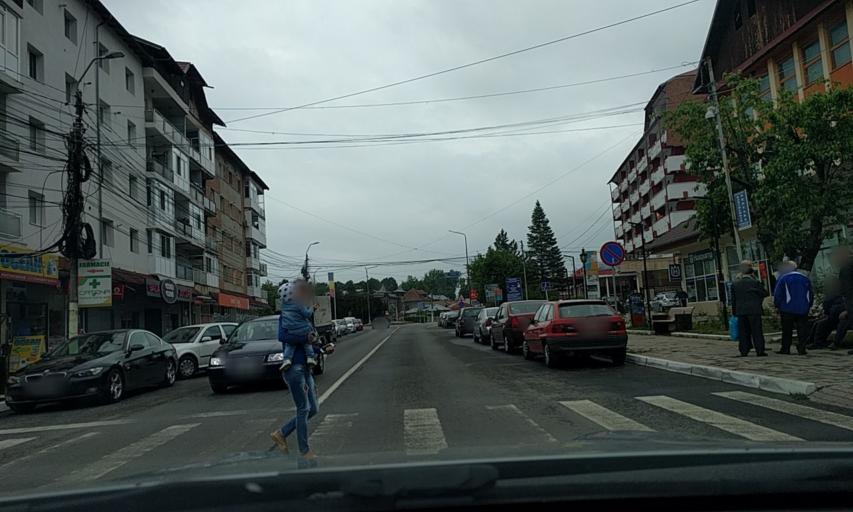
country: RO
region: Dambovita
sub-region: Oras Pucioasa
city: Pucioasa
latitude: 45.0770
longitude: 25.4341
